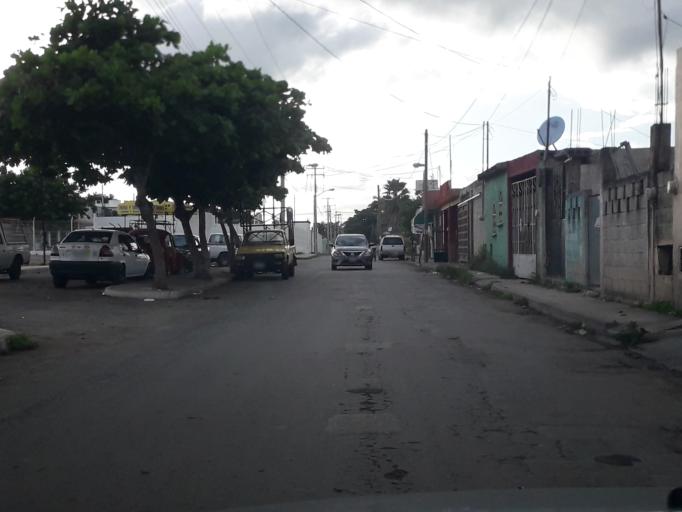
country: MX
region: Yucatan
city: Merida
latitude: 20.9608
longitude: -89.6600
